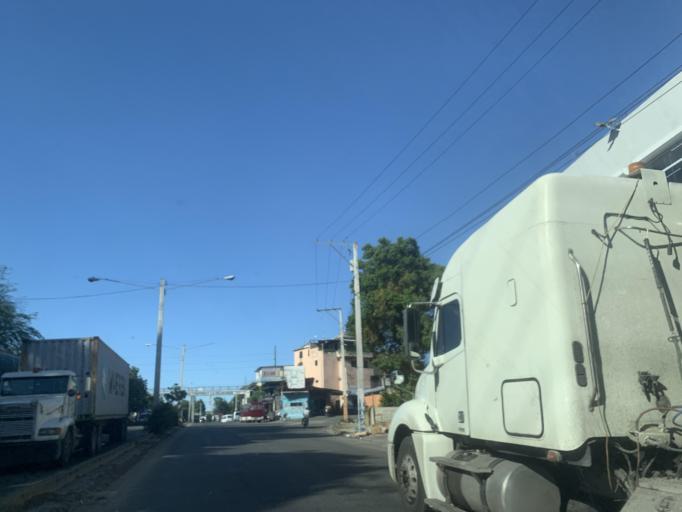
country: DO
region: San Cristobal
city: Bajos de Haina
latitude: 18.4310
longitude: -70.0270
